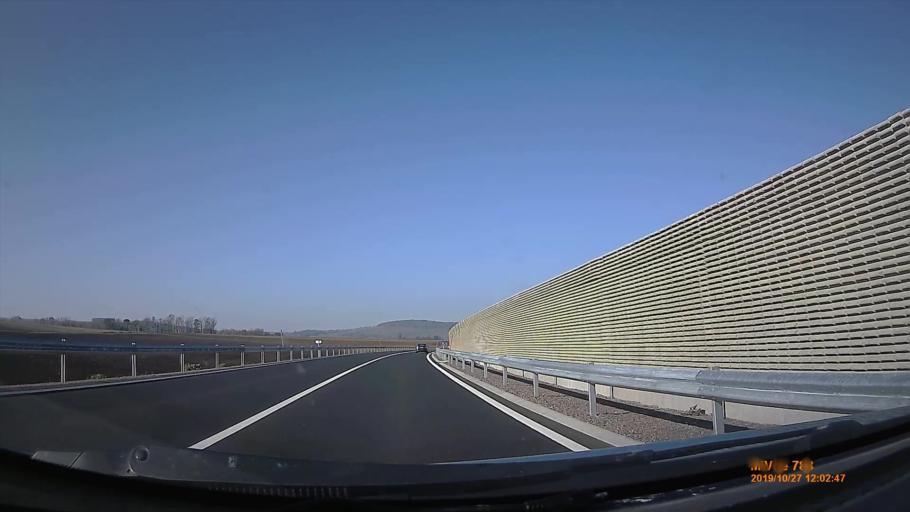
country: AT
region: Lower Austria
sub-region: Politischer Bezirk Mistelbach
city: Drasenhofen
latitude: 48.7369
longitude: 16.6456
